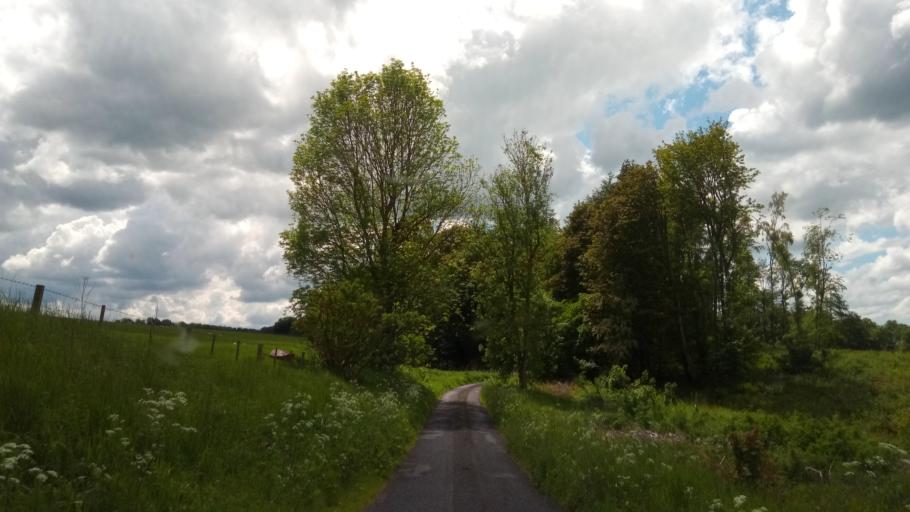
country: GB
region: Scotland
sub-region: The Scottish Borders
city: Coldstream
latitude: 55.5927
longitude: -2.2874
